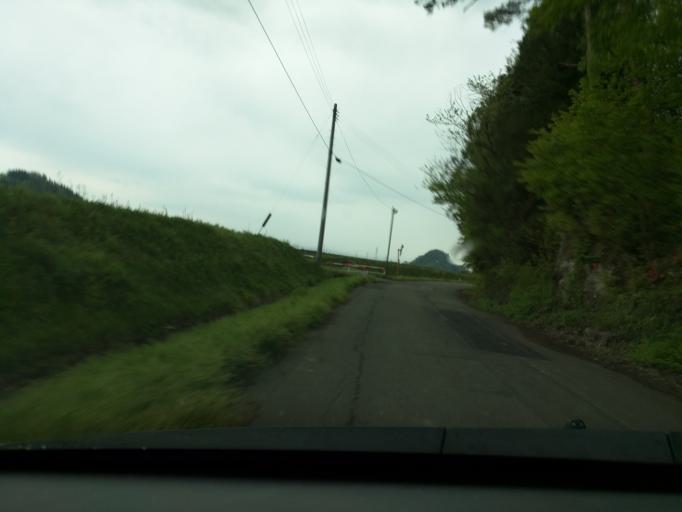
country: JP
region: Fukushima
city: Kitakata
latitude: 37.4295
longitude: 139.8881
